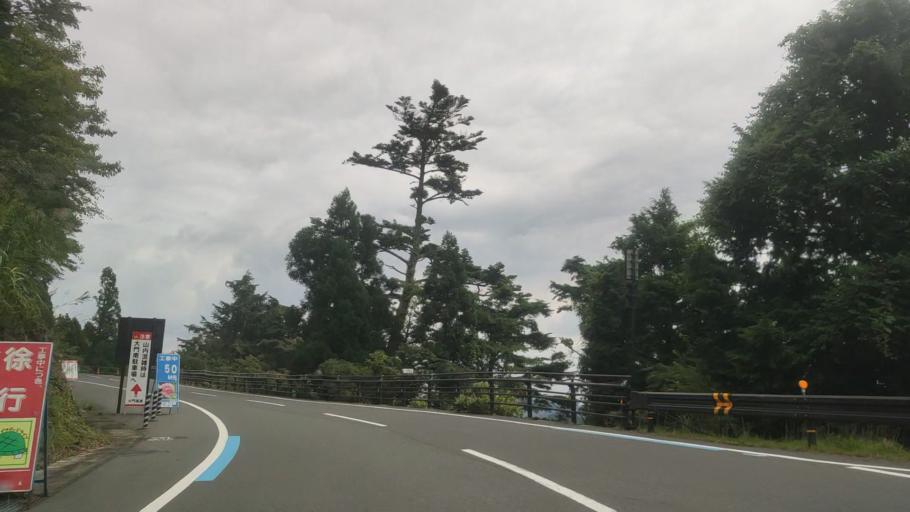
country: JP
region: Wakayama
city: Koya
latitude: 34.2179
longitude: 135.5673
